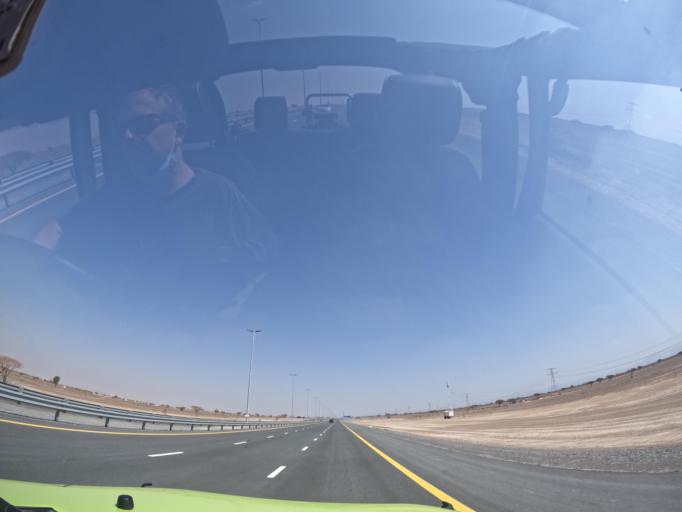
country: AE
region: Ash Shariqah
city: Adh Dhayd
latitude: 24.9487
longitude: 55.8330
